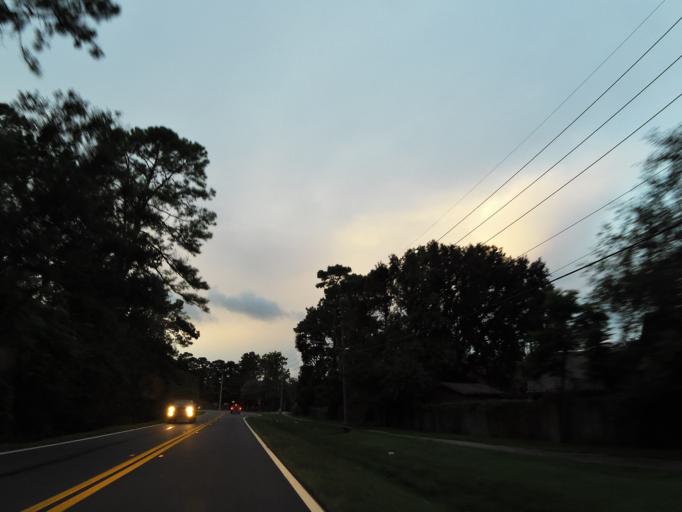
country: US
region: Florida
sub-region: Duval County
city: Jacksonville
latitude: 30.3790
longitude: -81.6075
